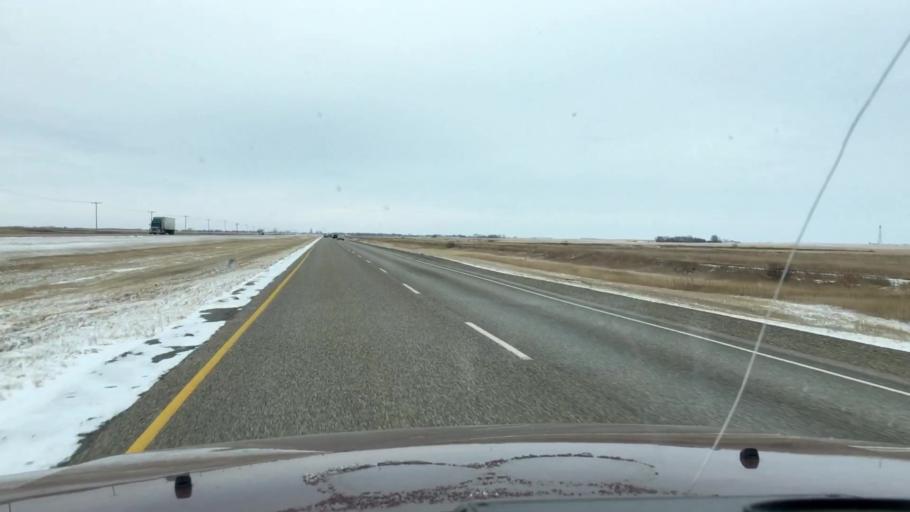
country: CA
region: Saskatchewan
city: Watrous
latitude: 51.0878
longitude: -105.8552
